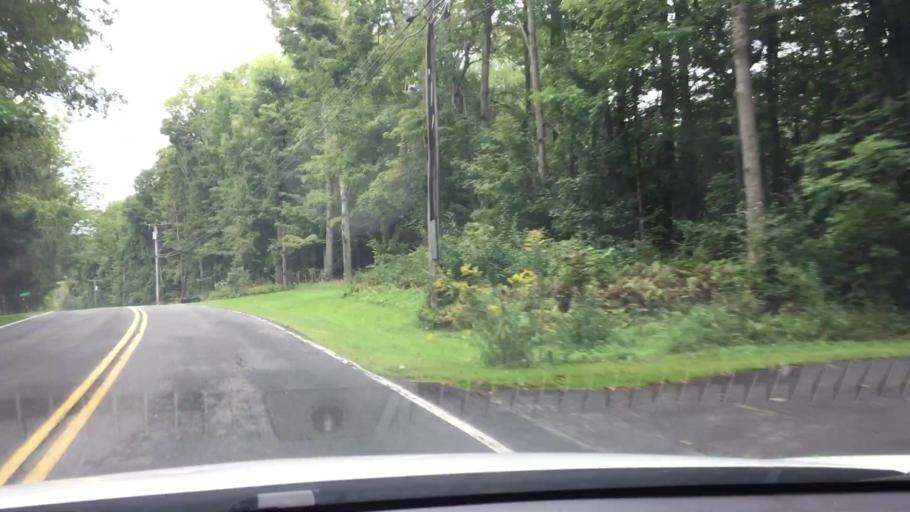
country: US
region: Massachusetts
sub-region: Berkshire County
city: Richmond
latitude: 42.3960
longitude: -73.3527
